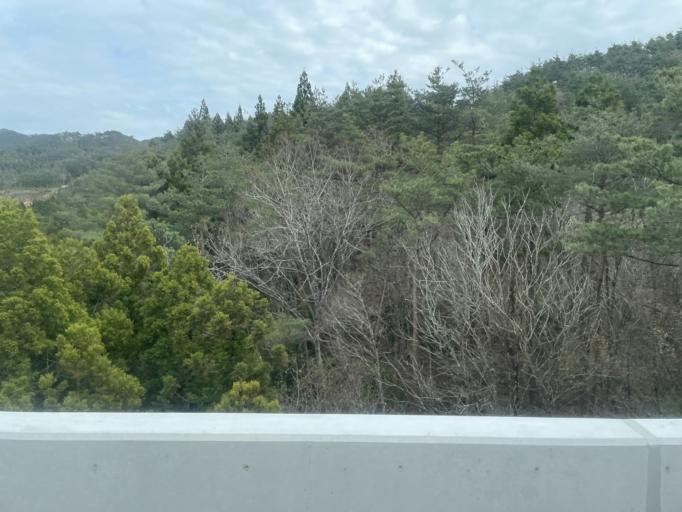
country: JP
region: Iwate
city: Ofunato
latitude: 38.9190
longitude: 141.5929
